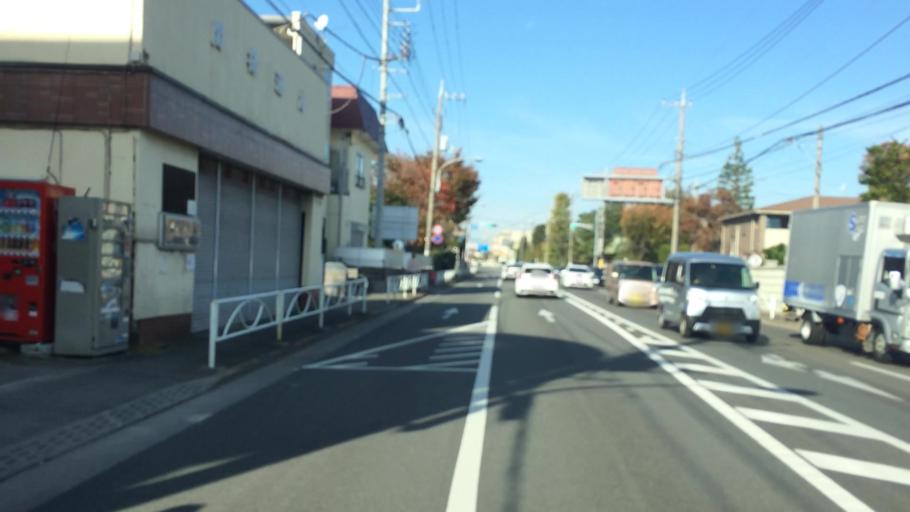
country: JP
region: Tokyo
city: Kokubunji
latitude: 35.6782
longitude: 139.4491
